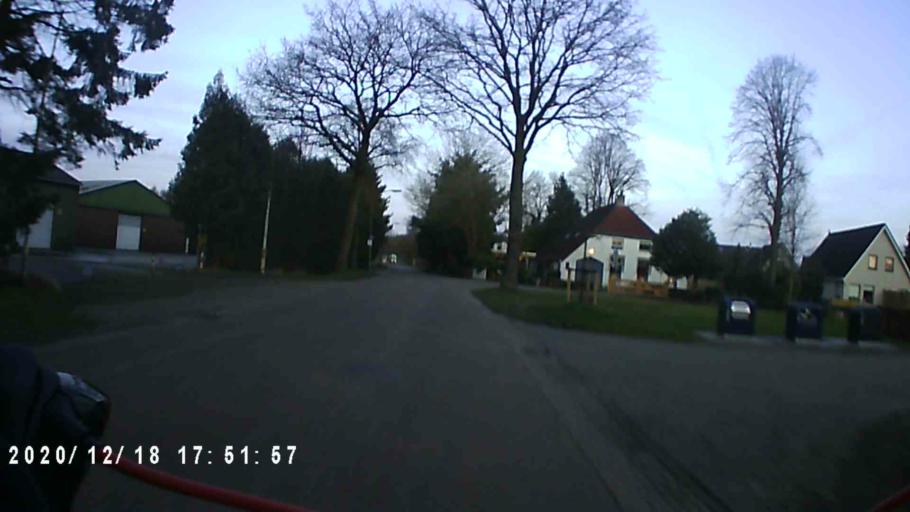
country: NL
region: Drenthe
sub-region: Gemeente Tynaarlo
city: Vries
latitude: 53.1174
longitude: 6.5933
